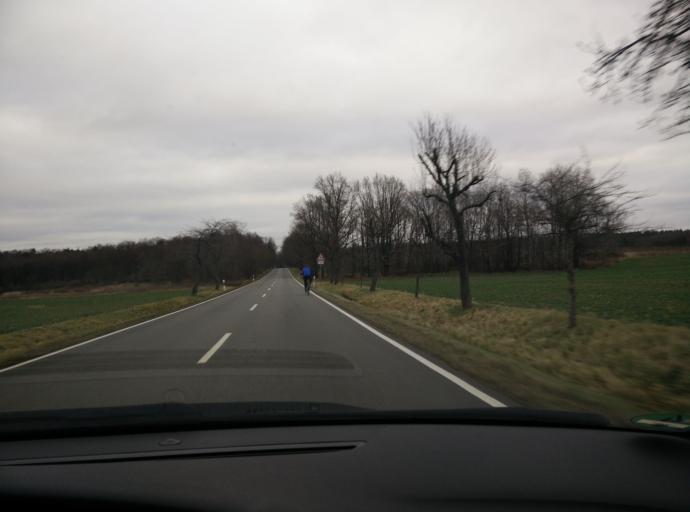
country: DE
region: Saxony
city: Bad Lausick
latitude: 51.1307
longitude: 12.6007
